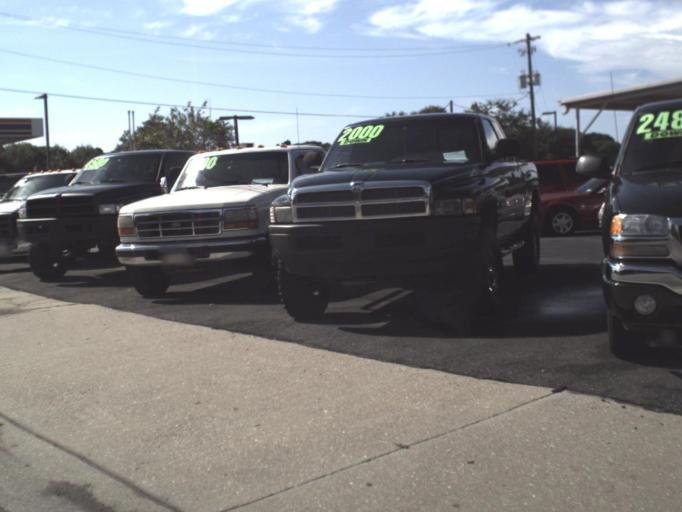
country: US
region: Florida
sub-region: Sarasota County
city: Gulf Gate Estates
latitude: 27.2657
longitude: -82.5276
